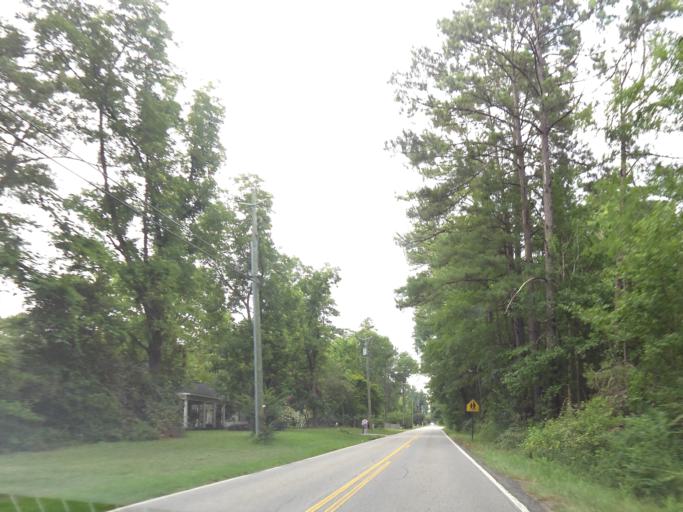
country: US
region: Georgia
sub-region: Bibb County
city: West Point
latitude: 32.9005
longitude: -83.7745
